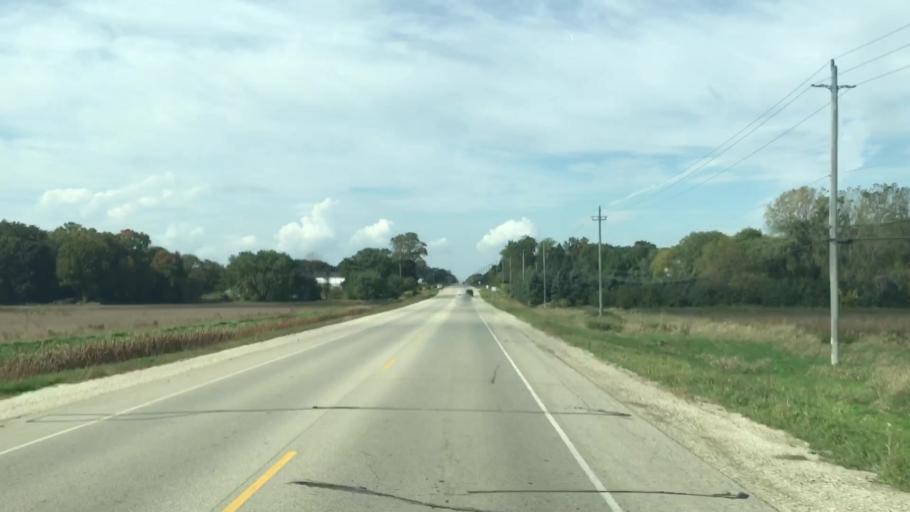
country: US
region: Wisconsin
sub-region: Ozaukee County
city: Mequon
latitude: 43.2215
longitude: -88.0290
